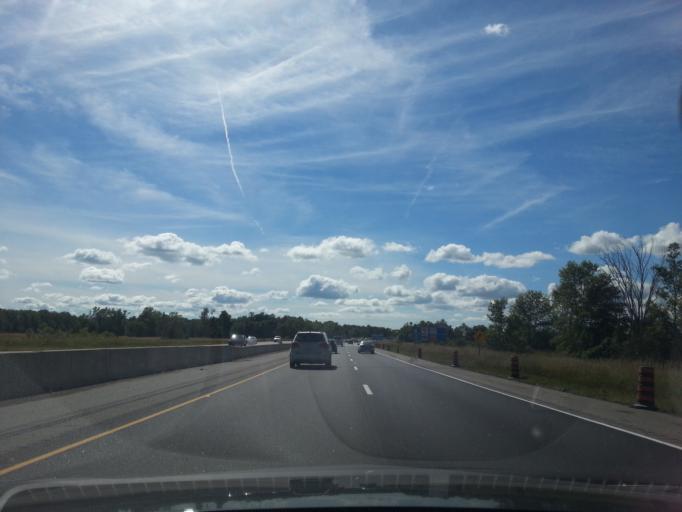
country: CA
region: Ontario
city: Skatepark
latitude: 44.2674
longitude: -76.9336
